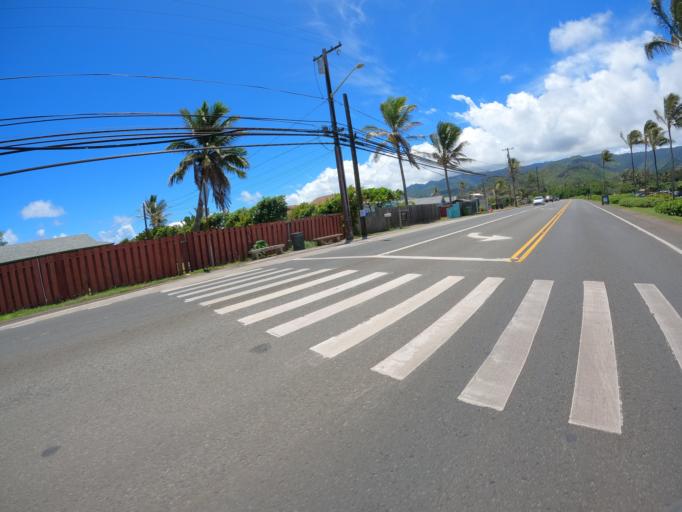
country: US
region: Hawaii
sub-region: Honolulu County
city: La'ie
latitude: 21.6388
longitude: -157.9197
